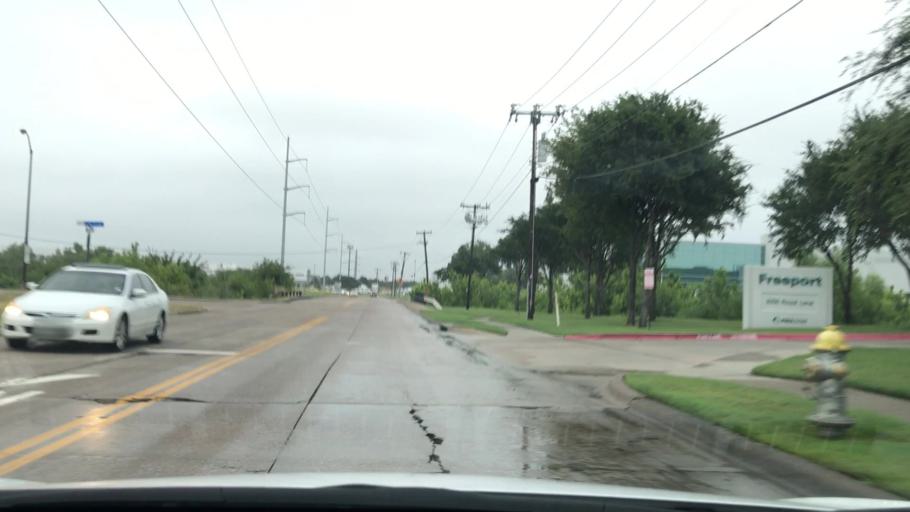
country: US
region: Texas
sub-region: Dallas County
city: Coppell
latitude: 32.9374
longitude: -97.0198
